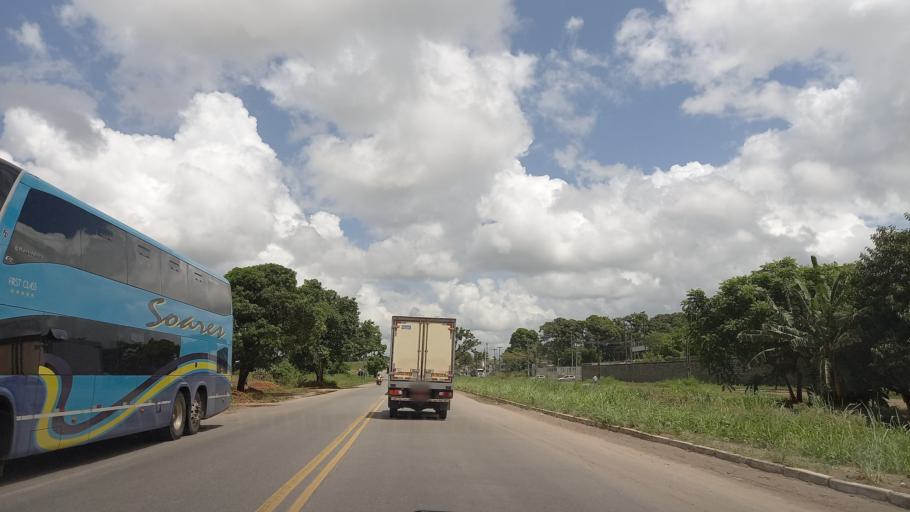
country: BR
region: Pernambuco
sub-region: Cabo De Santo Agostinho
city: Cabo
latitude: -8.2485
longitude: -35.0014
